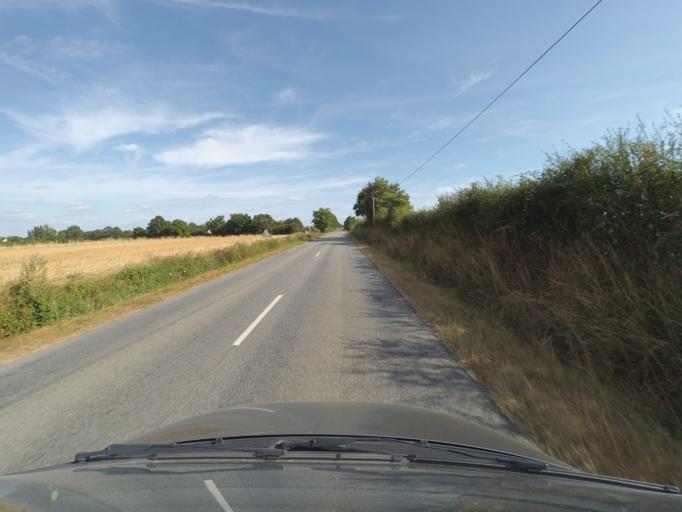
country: FR
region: Pays de la Loire
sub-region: Departement de la Loire-Atlantique
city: Vieillevigne
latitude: 46.9883
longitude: -1.4464
